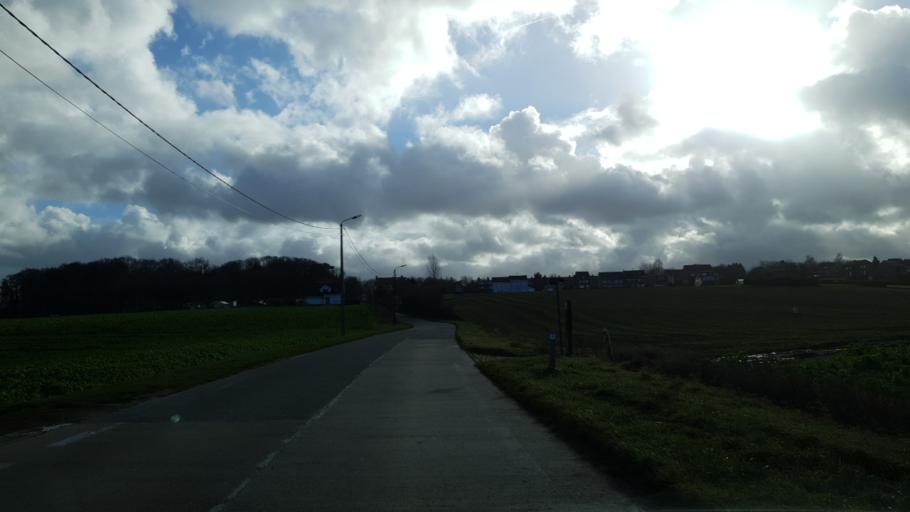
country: BE
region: Flanders
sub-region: Provincie Vlaams-Brabant
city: Bertem
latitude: 50.8572
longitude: 4.5846
